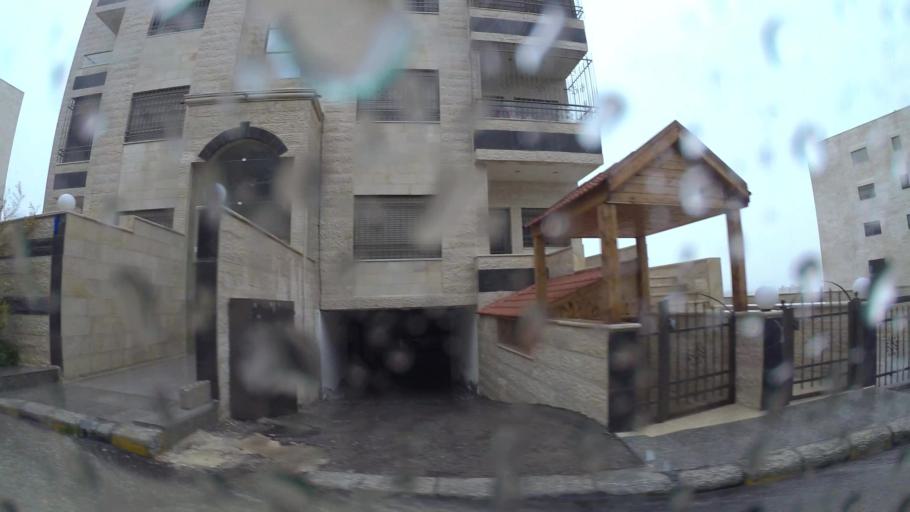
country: JO
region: Amman
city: Al Jubayhah
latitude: 32.0307
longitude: 35.8911
